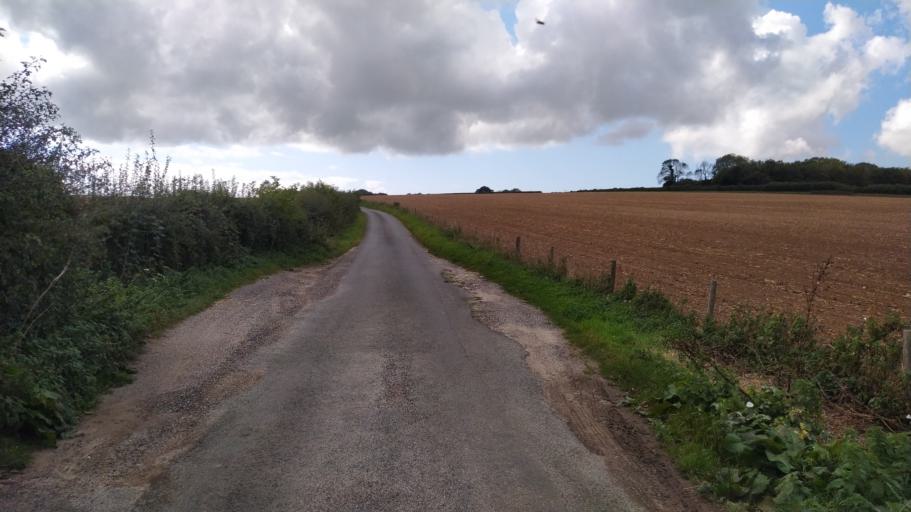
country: GB
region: England
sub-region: Dorset
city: Dorchester
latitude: 50.6765
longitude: -2.4177
